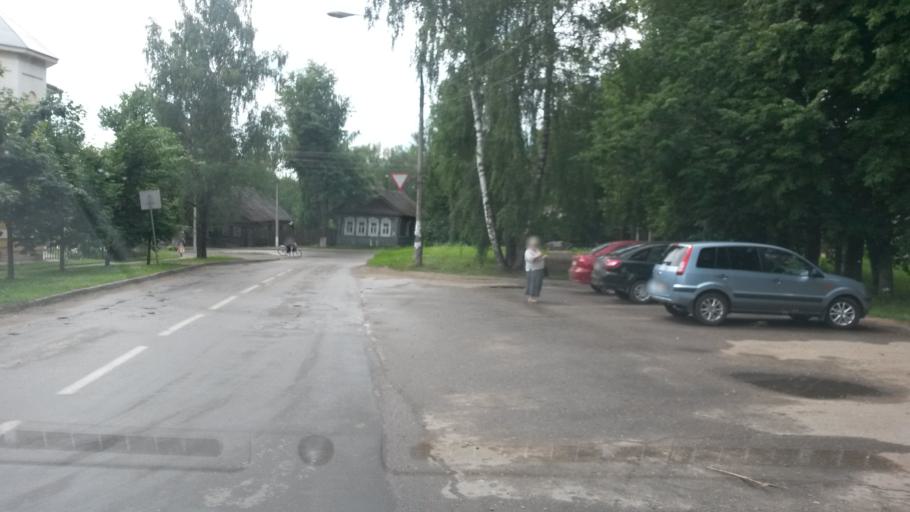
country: RU
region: Jaroslavl
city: Gavrilov-Yam
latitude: 57.3076
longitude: 39.8528
